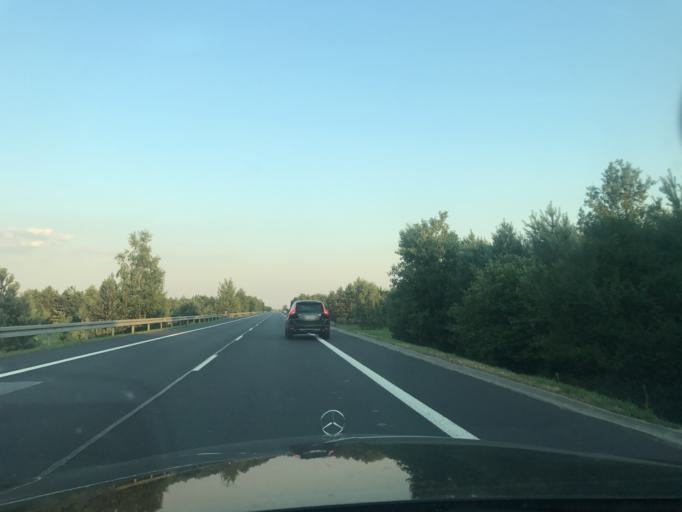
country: PL
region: Lublin Voivodeship
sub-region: Powiat lubartowski
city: Lubartow
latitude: 51.4461
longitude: 22.5836
